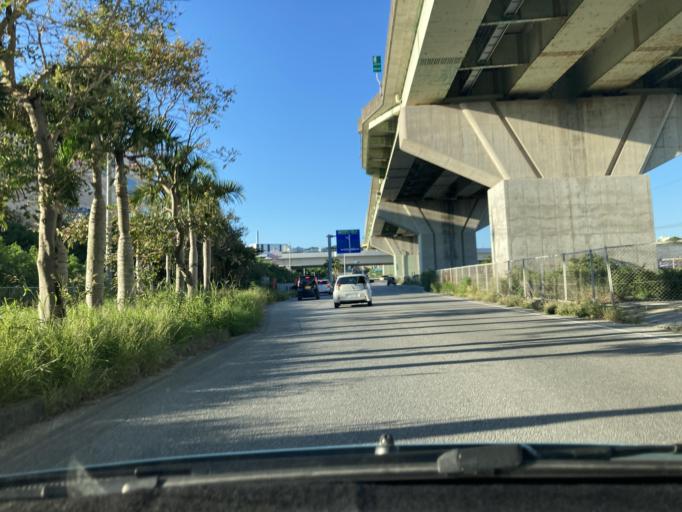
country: JP
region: Okinawa
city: Tomigusuku
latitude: 26.2007
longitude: 127.7393
